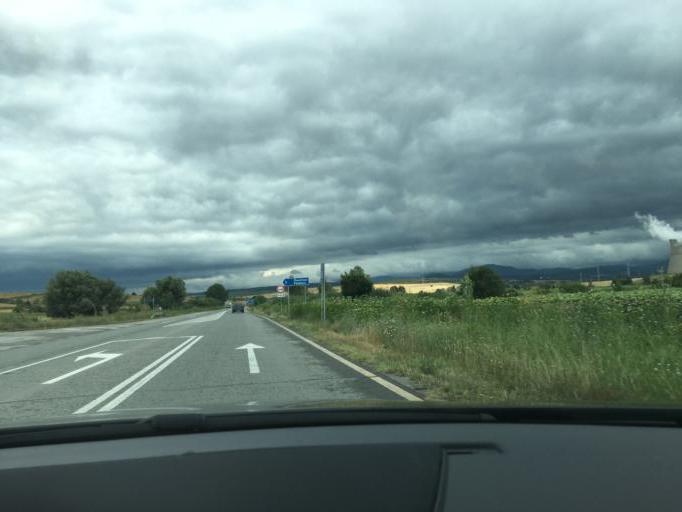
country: BG
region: Kyustendil
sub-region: Obshtina Dupnitsa
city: Dupnitsa
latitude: 42.2702
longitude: 23.0440
